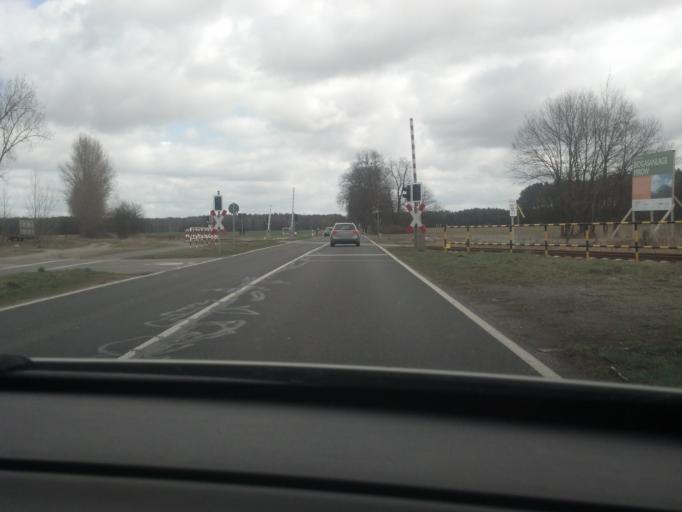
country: DE
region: Mecklenburg-Vorpommern
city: Rechlin
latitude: 53.2726
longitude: 12.8309
